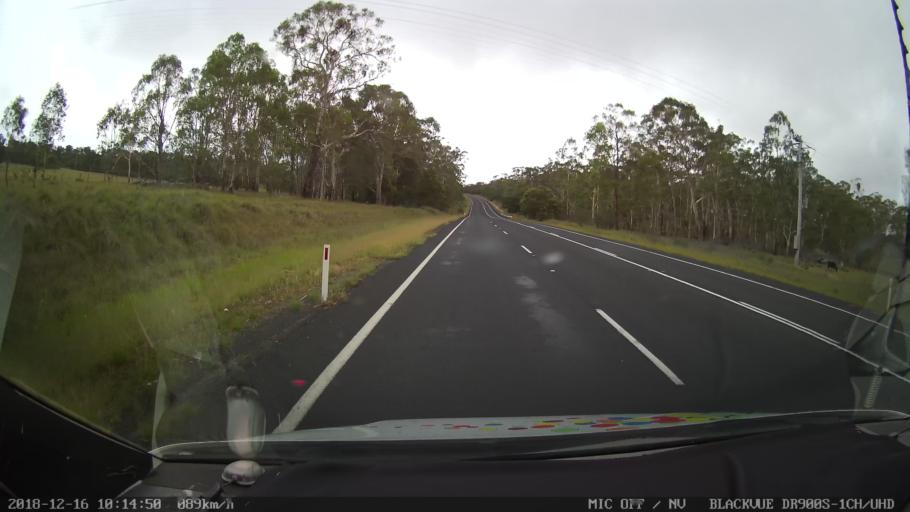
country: AU
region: New South Wales
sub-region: Tenterfield Municipality
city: Carrolls Creek
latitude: -29.2829
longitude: 151.9664
